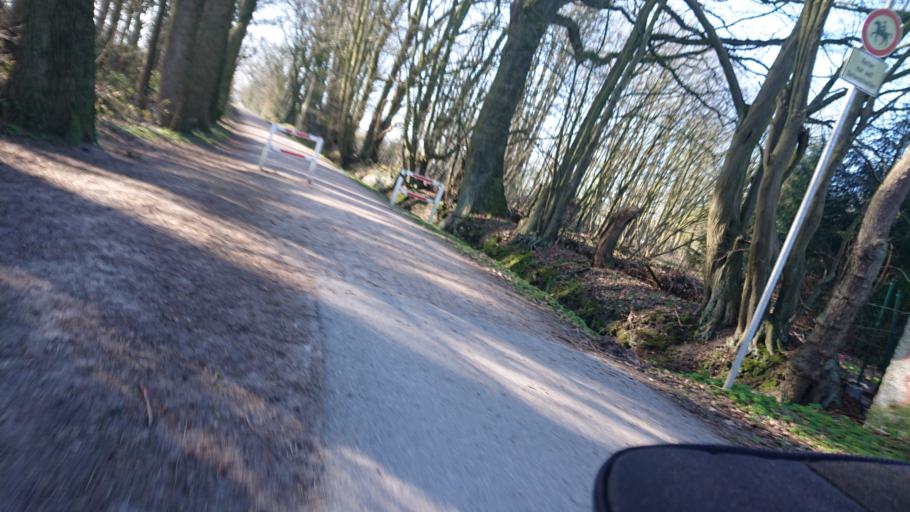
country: DE
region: Schleswig-Holstein
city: Ellerbek
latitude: 53.6524
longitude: 9.8846
